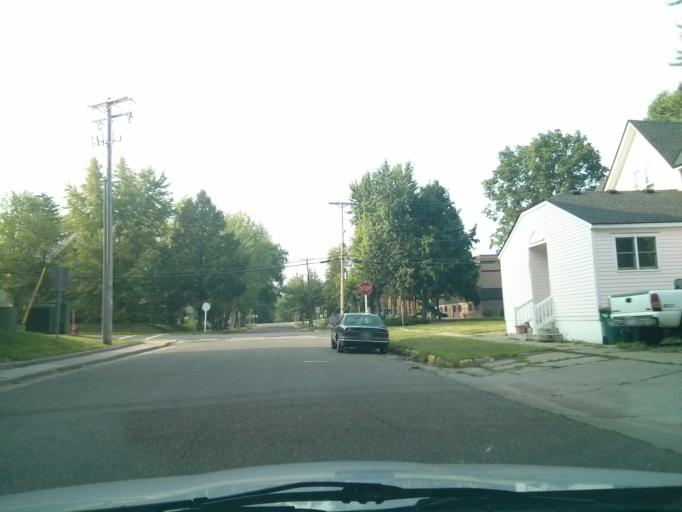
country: US
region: Wisconsin
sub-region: Saint Croix County
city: Hudson
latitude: 44.9820
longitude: -92.7525
